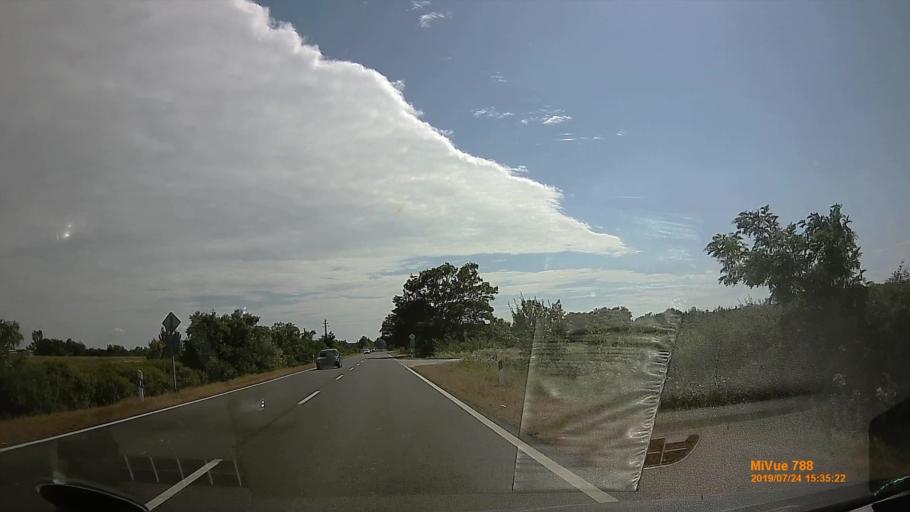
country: HU
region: Szabolcs-Szatmar-Bereg
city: Vasarosnameny
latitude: 48.1379
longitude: 22.3568
